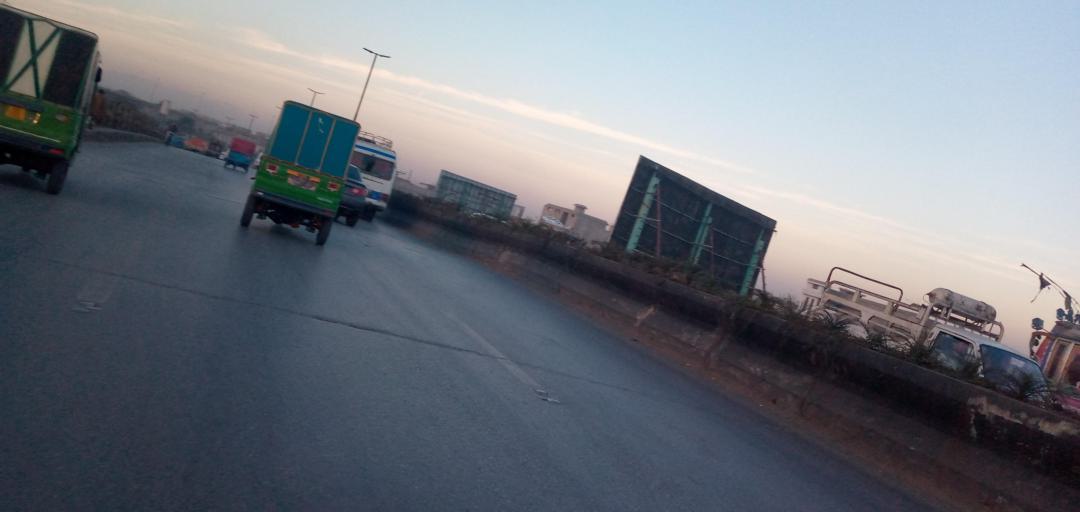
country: PK
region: Khyber Pakhtunkhwa
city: Peshawar
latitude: 34.0196
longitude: 71.6217
